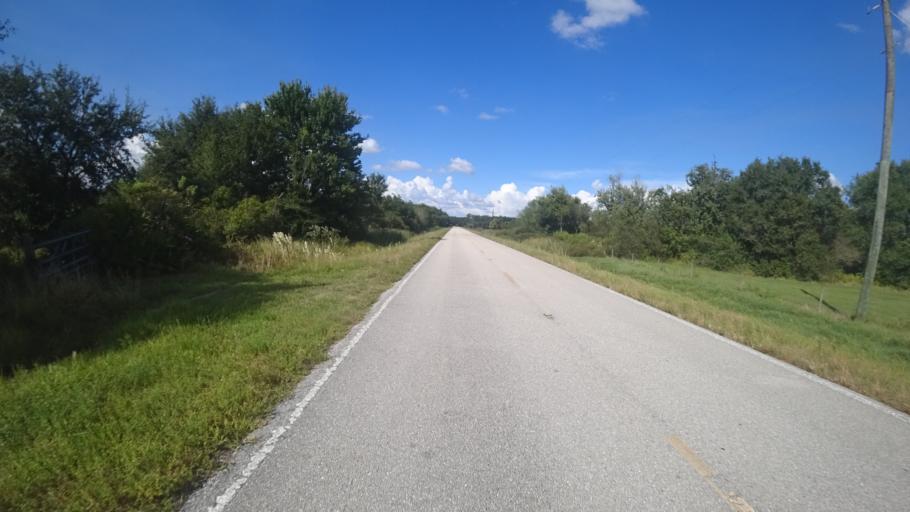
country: US
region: Florida
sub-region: DeSoto County
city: Arcadia
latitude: 27.2878
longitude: -82.0563
